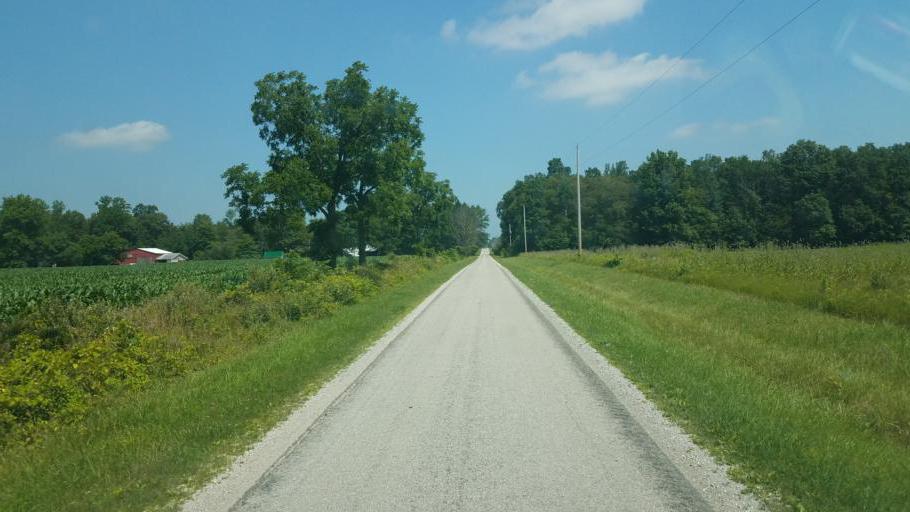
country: US
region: Ohio
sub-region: Seneca County
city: Tiffin
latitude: 41.0418
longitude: -82.9771
